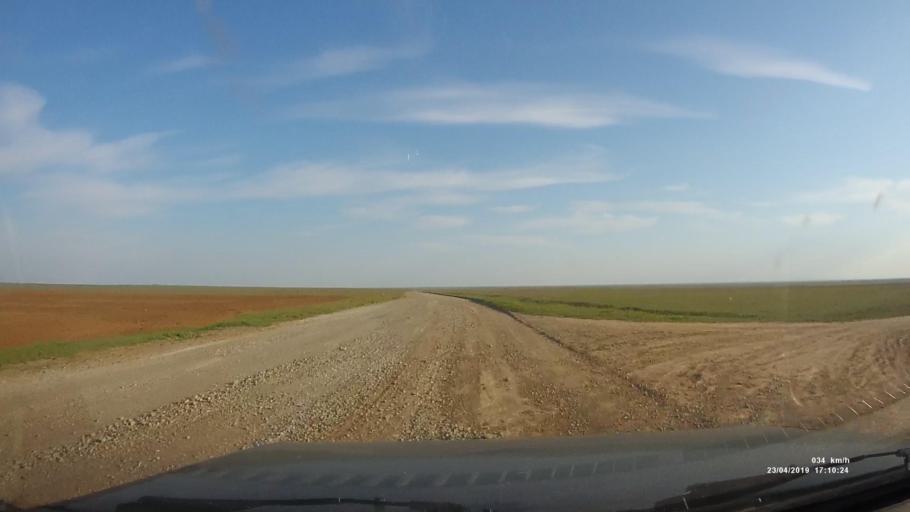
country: RU
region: Kalmykiya
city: Priyutnoye
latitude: 46.2469
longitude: 43.4841
